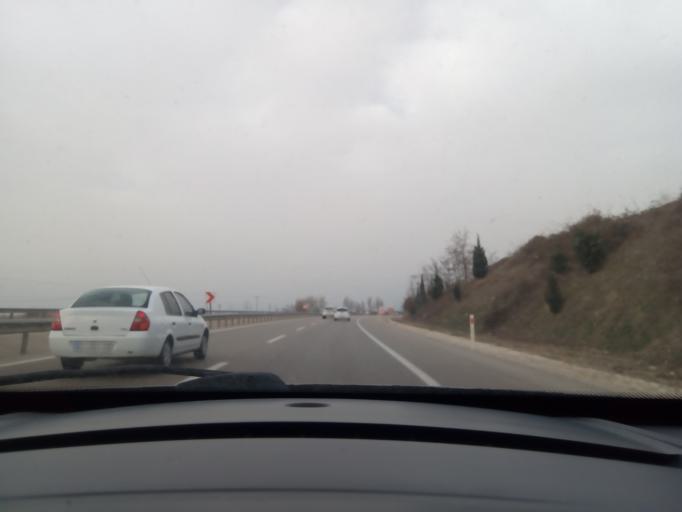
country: TR
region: Bursa
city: Mahmudiye
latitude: 40.2085
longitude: 28.5975
